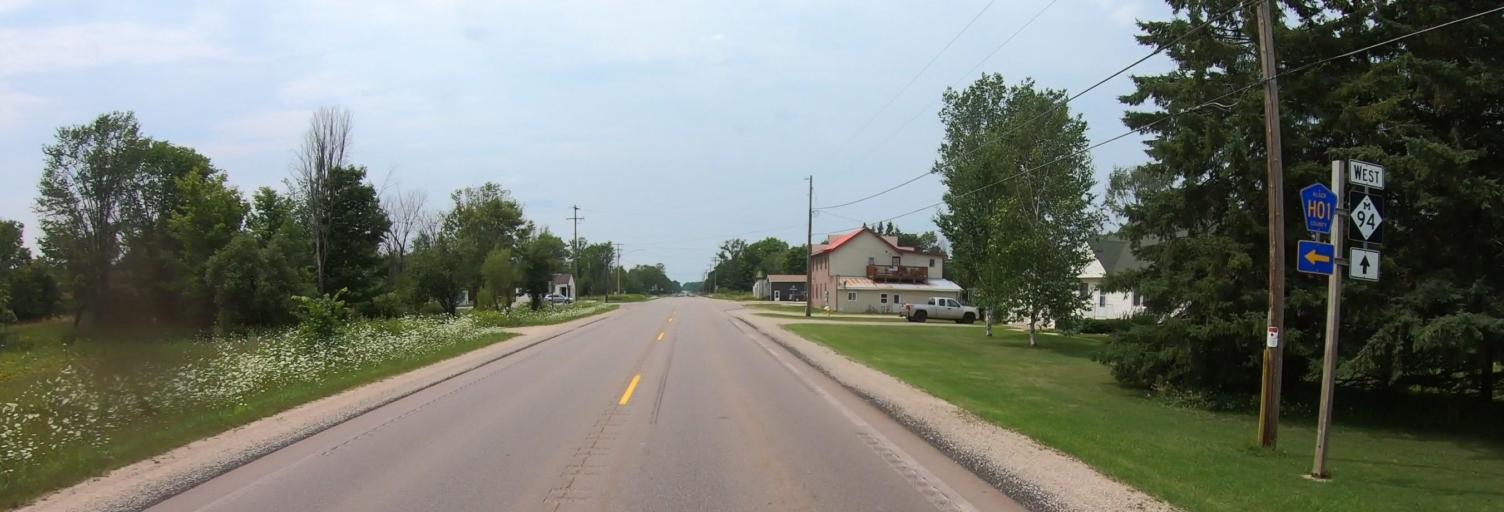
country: US
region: Michigan
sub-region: Alger County
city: Munising
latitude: 46.3549
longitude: -86.9695
